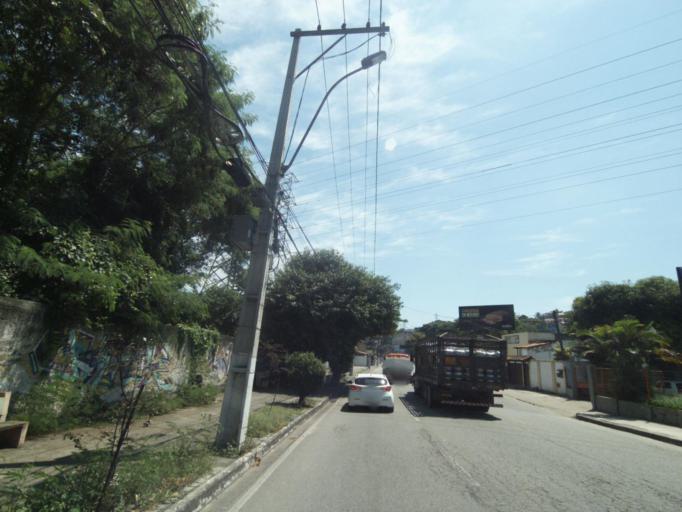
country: BR
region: Rio de Janeiro
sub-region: Niteroi
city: Niteroi
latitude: -22.9063
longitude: -43.0628
